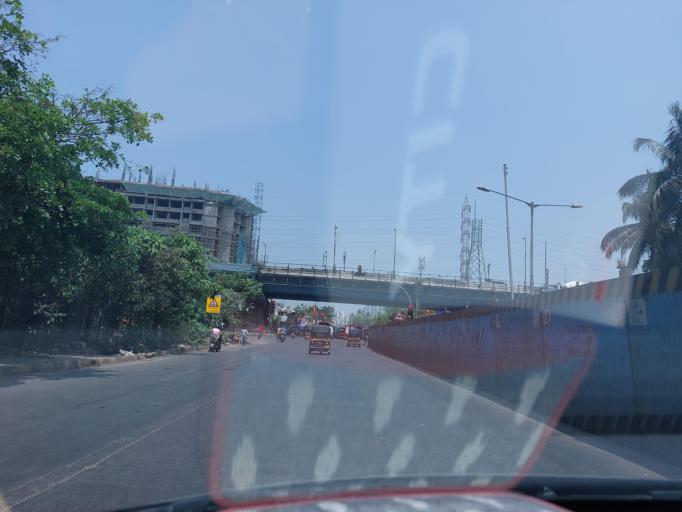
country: IN
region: Maharashtra
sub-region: Mumbai Suburban
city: Mumbai
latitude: 19.0561
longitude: 72.8878
